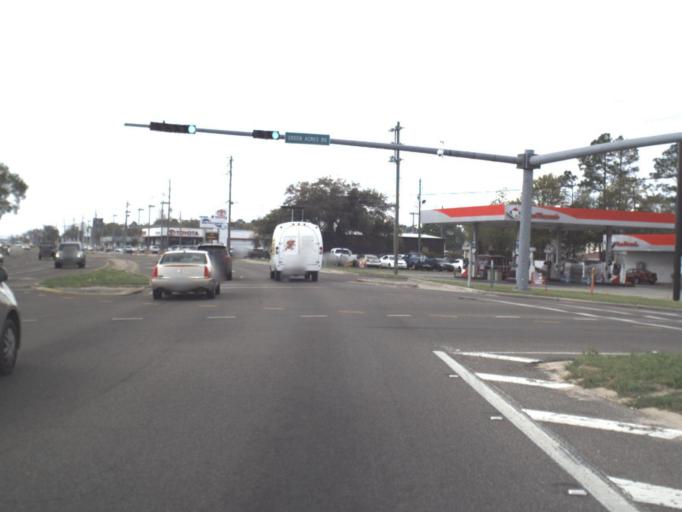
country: US
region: Florida
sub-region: Okaloosa County
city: Wright
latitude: 30.4561
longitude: -86.6383
